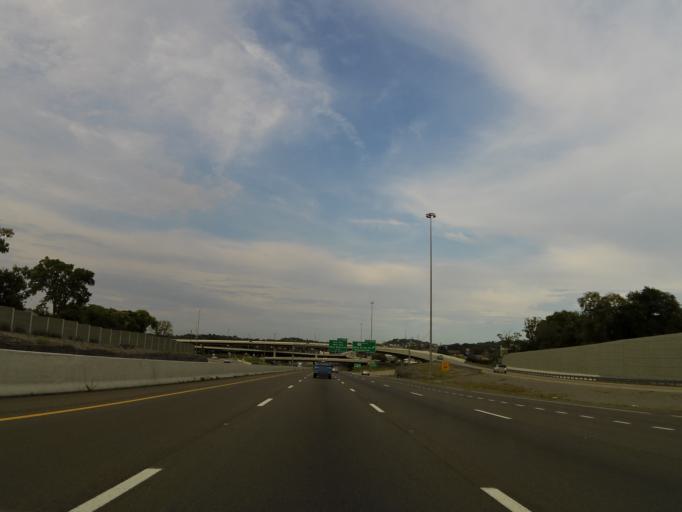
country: US
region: Tennessee
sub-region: Davidson County
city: Belle Meade
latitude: 36.1512
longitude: -86.8620
